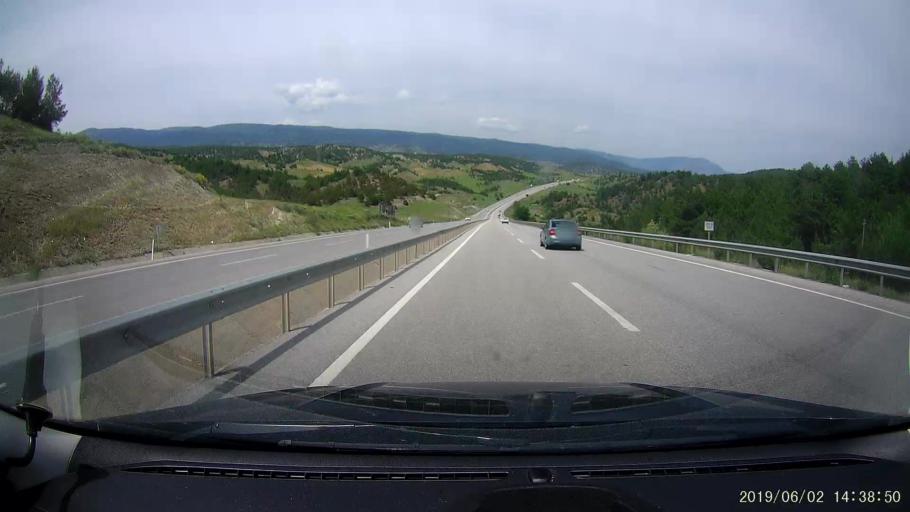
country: TR
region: Corum
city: Hacihamza
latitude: 41.0610
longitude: 34.2888
